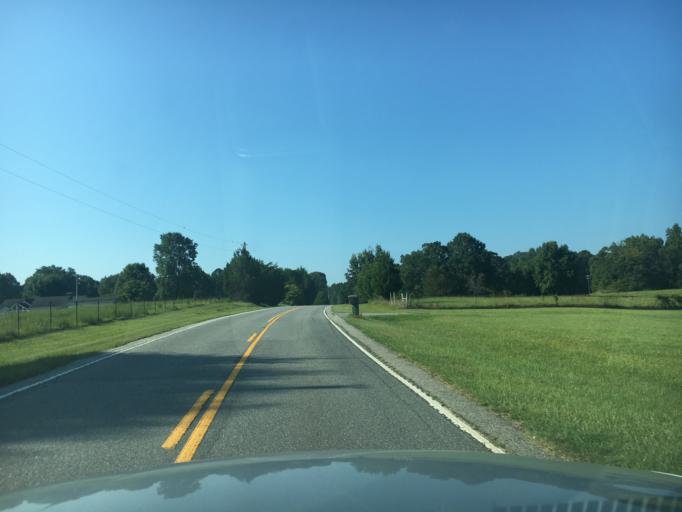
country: US
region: South Carolina
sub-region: Anderson County
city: Williamston
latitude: 34.6216
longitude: -82.3503
